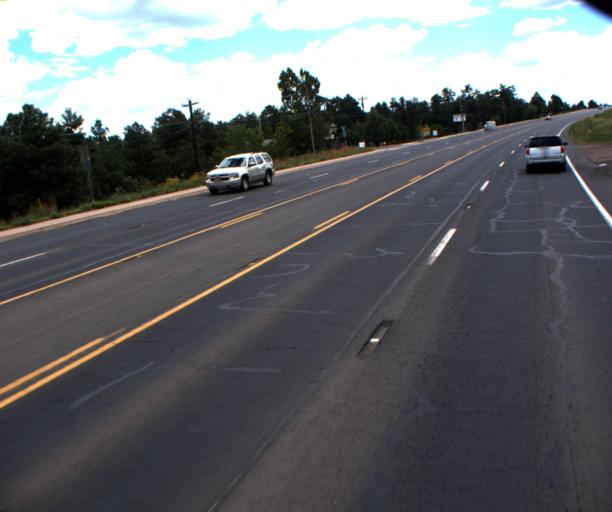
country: US
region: Arizona
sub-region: Navajo County
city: Show Low
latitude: 34.2072
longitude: -110.0219
